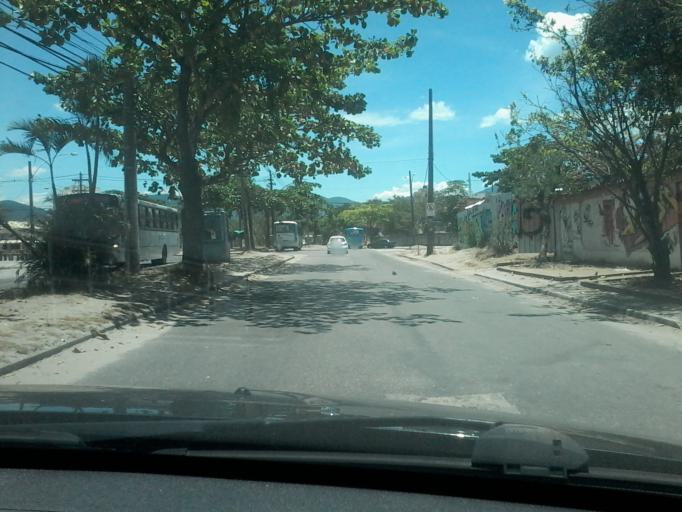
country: BR
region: Rio de Janeiro
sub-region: Nilopolis
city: Nilopolis
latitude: -23.0232
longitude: -43.4820
